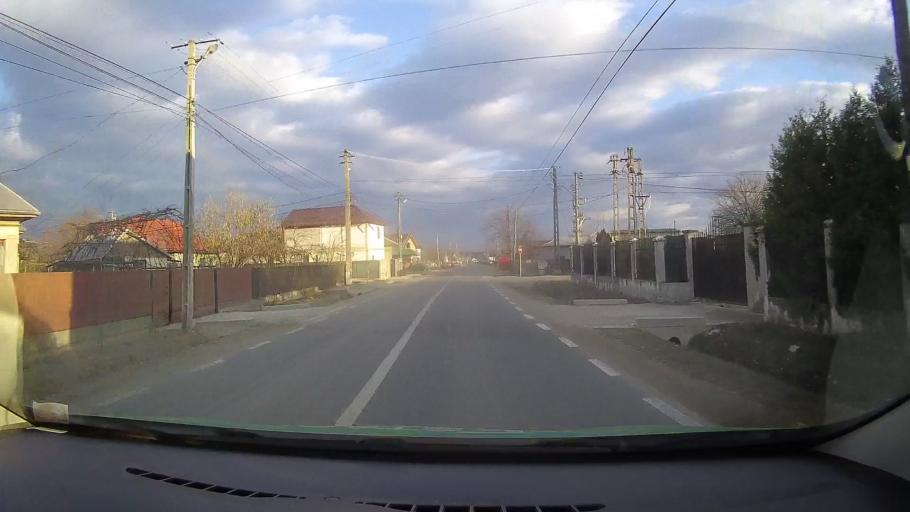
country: RO
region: Dambovita
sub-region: Comuna I. L. Caragiale
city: Ghirdoveni
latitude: 44.9447
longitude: 25.6645
